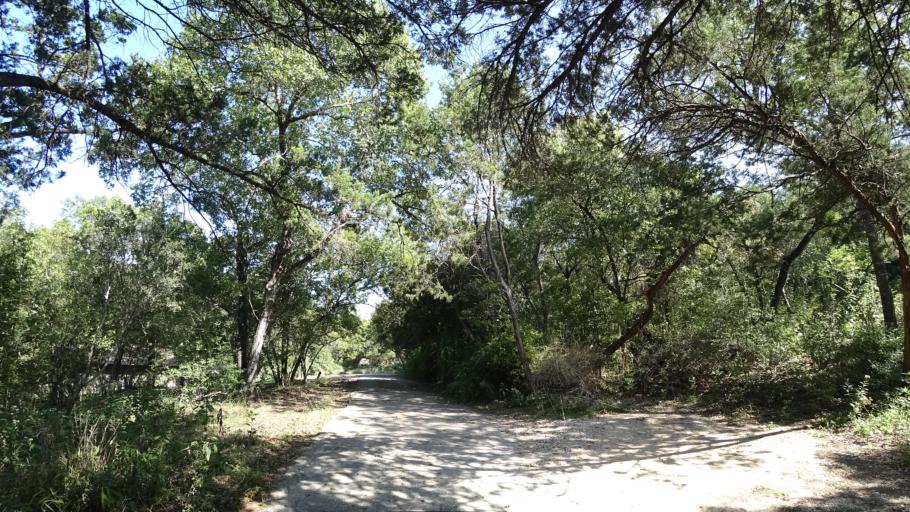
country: US
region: Texas
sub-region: Travis County
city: West Lake Hills
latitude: 30.2937
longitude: -97.8088
